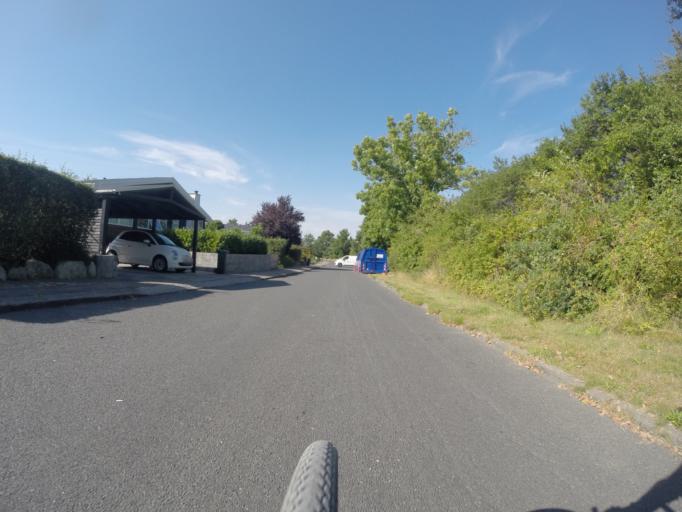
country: DK
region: Capital Region
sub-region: Herlev Kommune
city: Herlev
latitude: 55.7460
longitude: 12.4275
